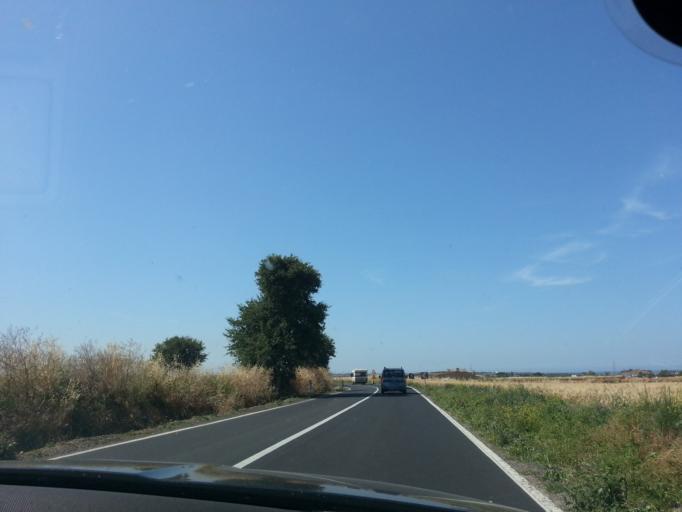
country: IT
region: Latium
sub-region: Provincia di Viterbo
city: Tarquinia
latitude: 42.2151
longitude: 11.7825
